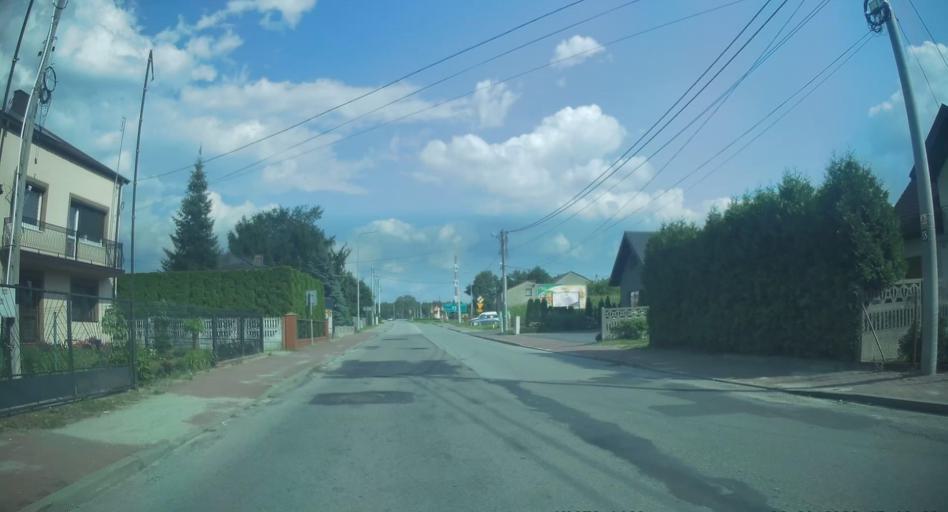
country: PL
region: Swietokrzyskie
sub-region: Powiat konecki
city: Radoszyce
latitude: 51.0722
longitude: 20.2657
